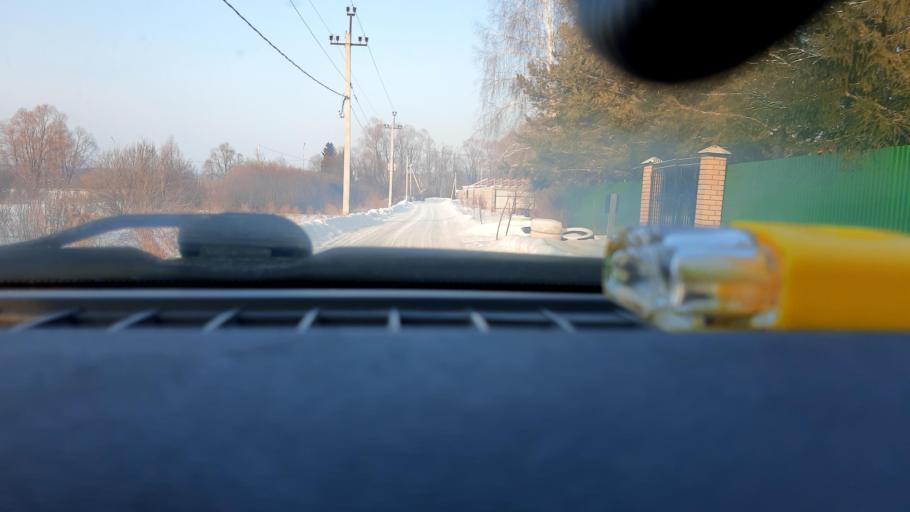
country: RU
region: Bashkortostan
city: Kabakovo
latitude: 54.6575
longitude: 56.1739
